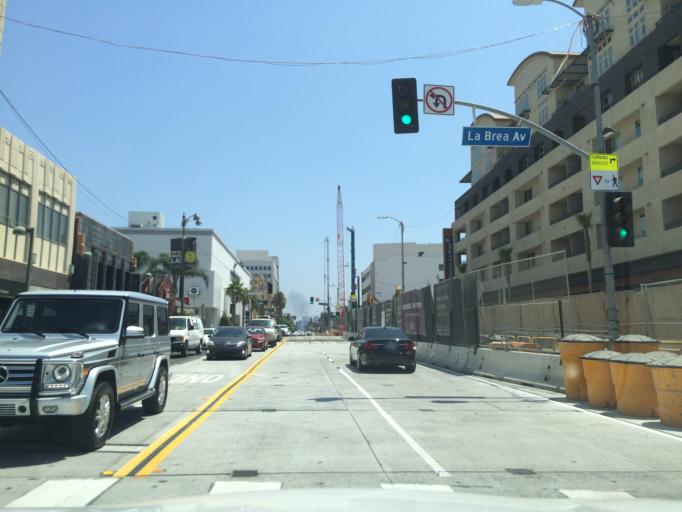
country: US
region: California
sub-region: Los Angeles County
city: West Hollywood
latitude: 34.0623
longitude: -118.3440
